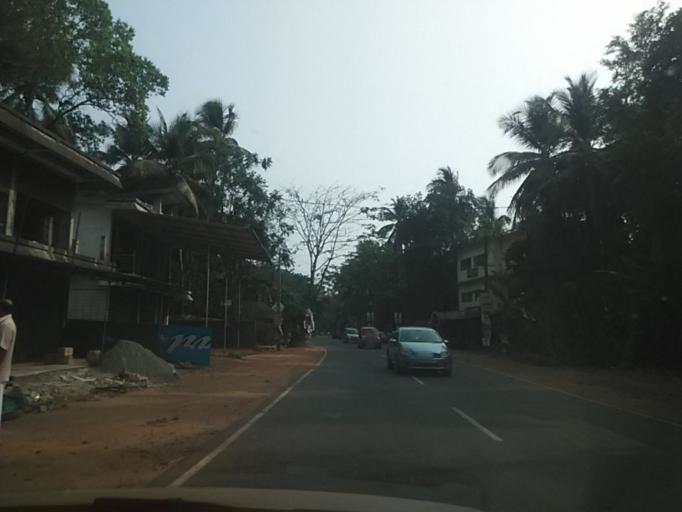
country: IN
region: Kerala
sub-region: Kozhikode
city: Naduvannur
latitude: 11.4826
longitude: 75.7748
